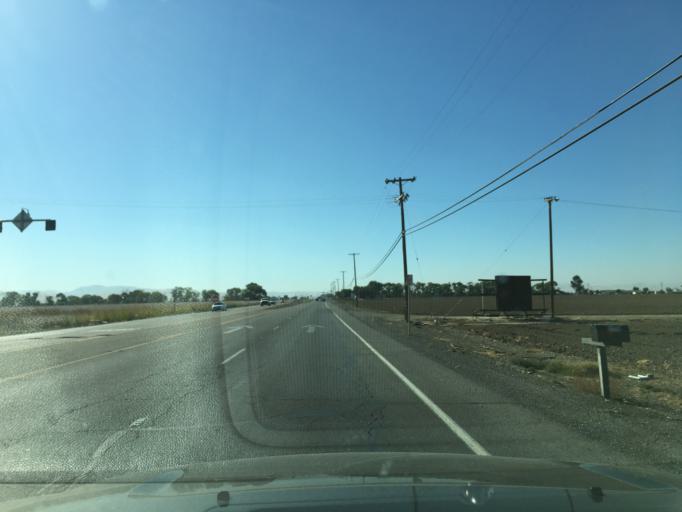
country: US
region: California
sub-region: Merced County
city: Los Banos
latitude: 37.0568
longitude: -120.8847
